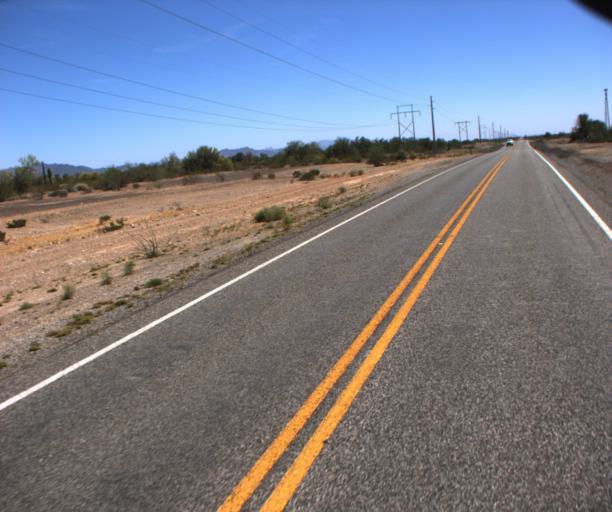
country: US
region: Arizona
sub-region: La Paz County
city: Quartzsite
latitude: 33.7140
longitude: -114.2171
